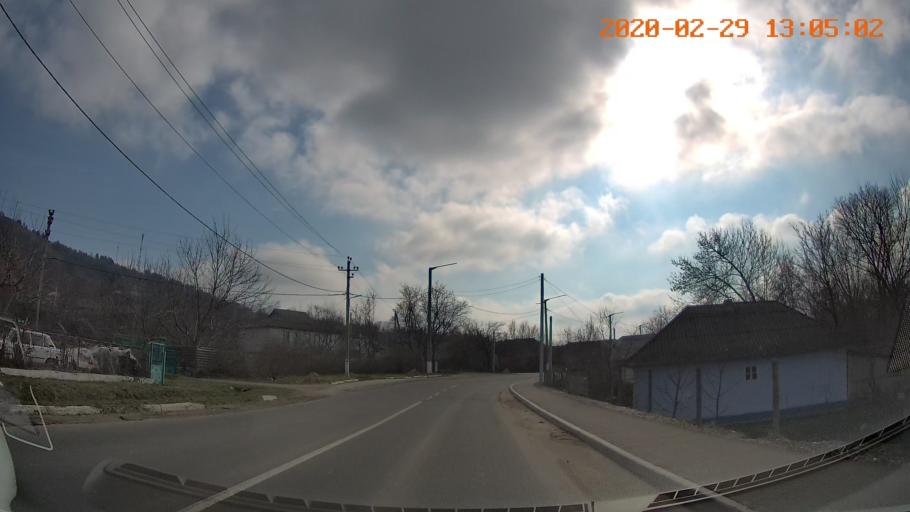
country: MD
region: Telenesti
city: Camenca
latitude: 48.0233
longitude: 28.7082
